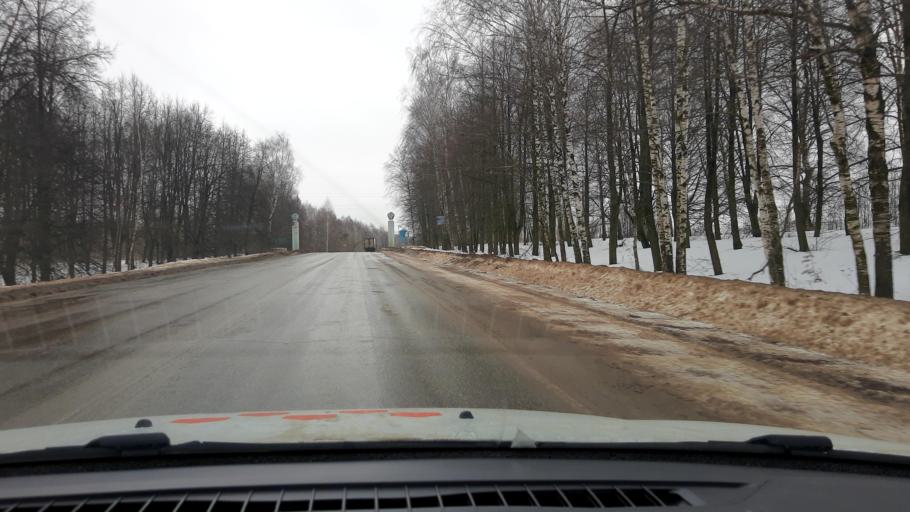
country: RU
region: Nizjnij Novgorod
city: Pavlovo
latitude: 55.9675
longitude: 43.1287
